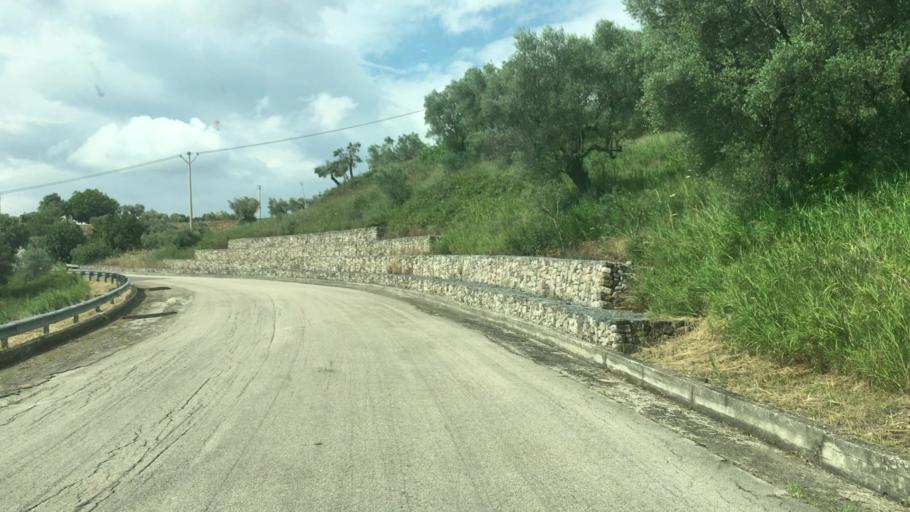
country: IT
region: Basilicate
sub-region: Provincia di Matera
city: San Mauro Forte
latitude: 40.4817
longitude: 16.2671
